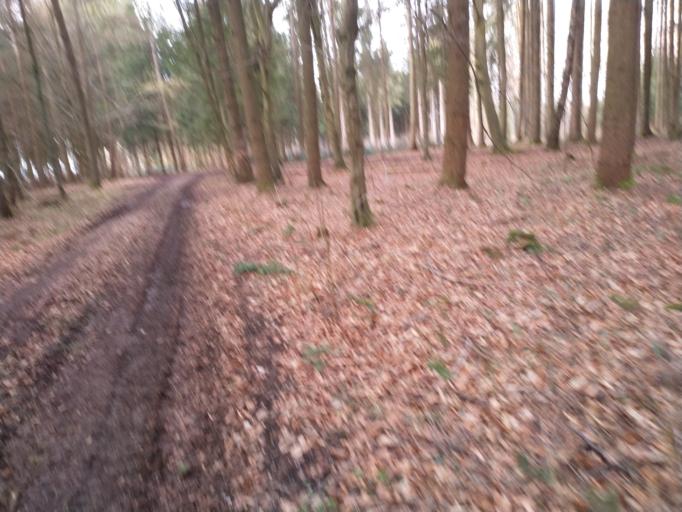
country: DE
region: Bavaria
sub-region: Swabia
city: Guenzburg
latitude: 48.4316
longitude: 10.3091
